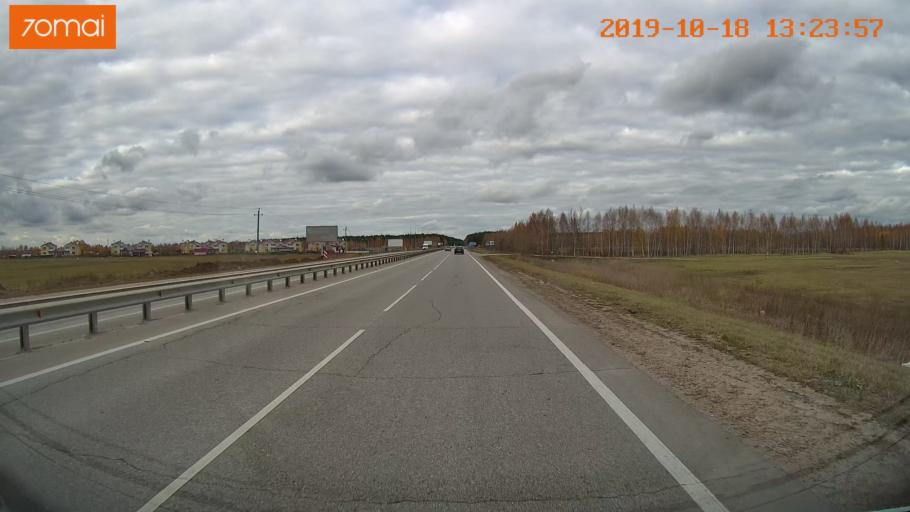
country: RU
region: Rjazan
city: Polyany
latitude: 54.7238
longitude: 39.8473
